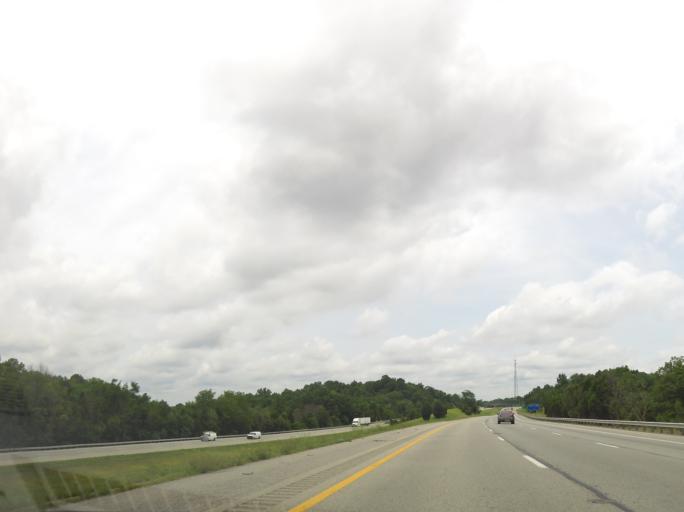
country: US
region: Kentucky
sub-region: Scott County
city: Georgetown
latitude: 38.3697
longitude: -84.5701
